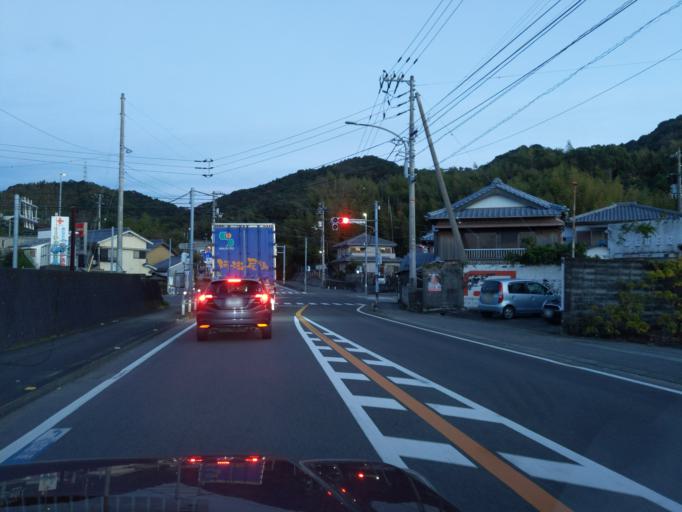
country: JP
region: Tokushima
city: Anan
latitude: 33.8728
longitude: 134.6377
